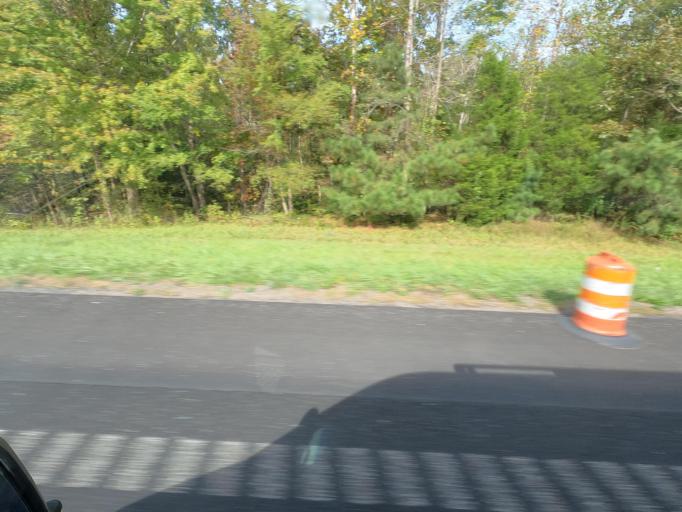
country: US
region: Tennessee
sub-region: Decatur County
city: Parsons
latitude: 35.8220
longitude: -88.1341
